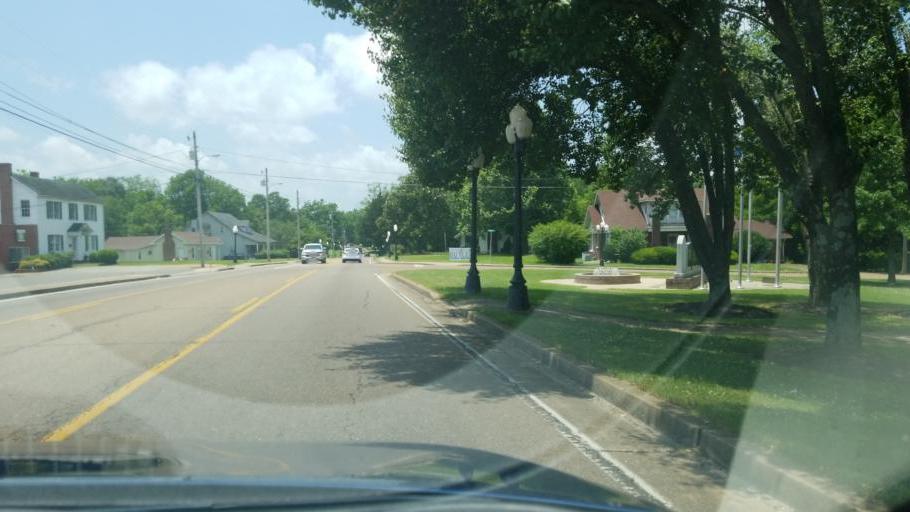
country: US
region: Tennessee
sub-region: Carroll County
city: Huntingdon
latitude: 36.0035
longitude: -88.4196
